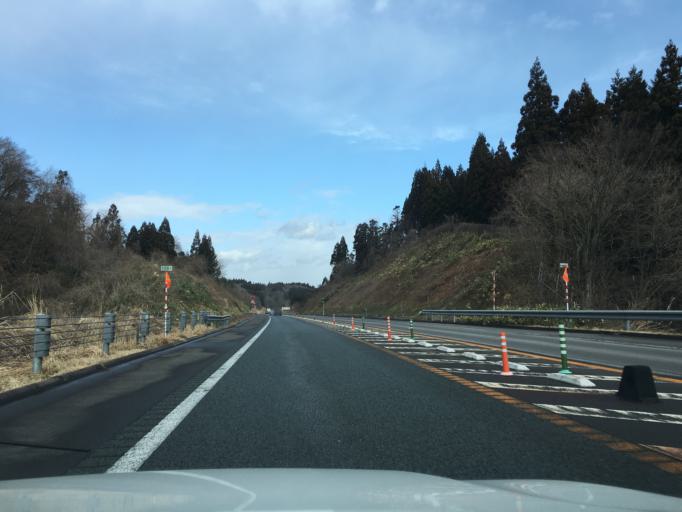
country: JP
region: Akita
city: Akita
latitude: 39.6720
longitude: 140.1876
